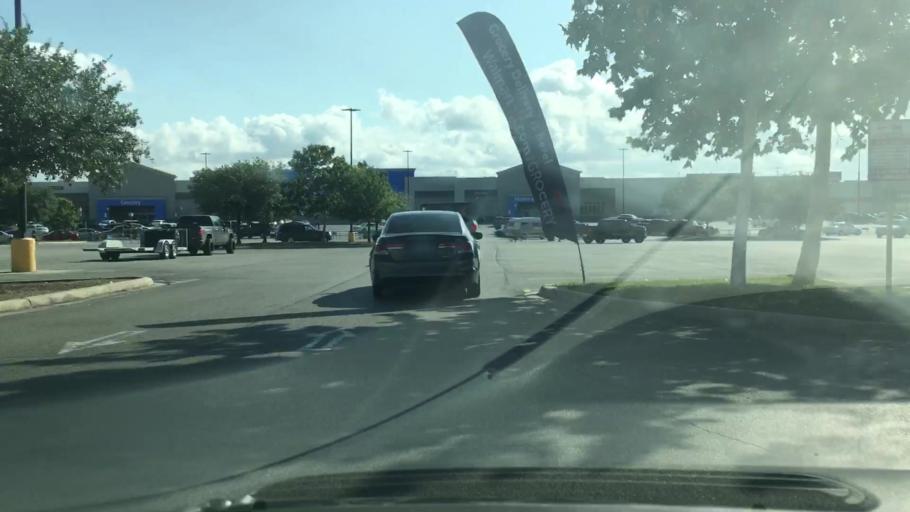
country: US
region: Texas
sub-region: Bexar County
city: Selma
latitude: 29.6030
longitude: -98.2770
